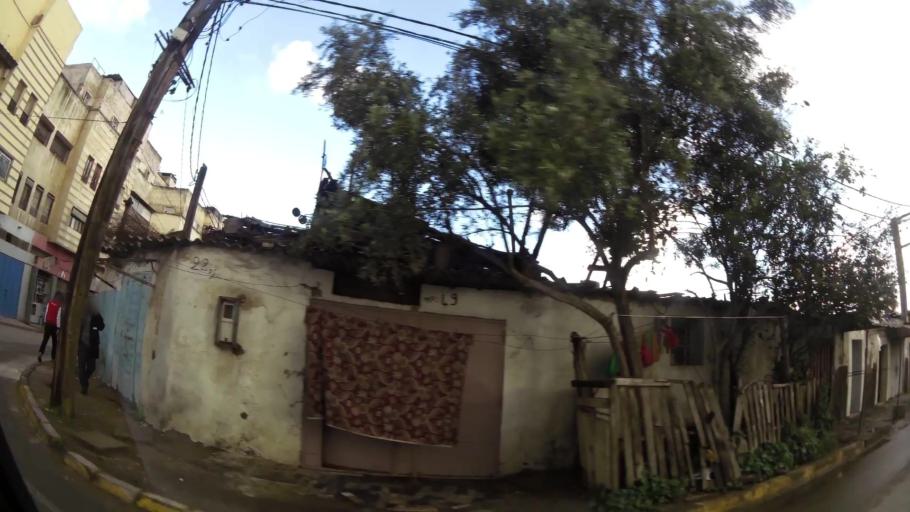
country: MA
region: Grand Casablanca
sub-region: Mediouna
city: Tit Mellil
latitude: 33.5810
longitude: -7.5348
